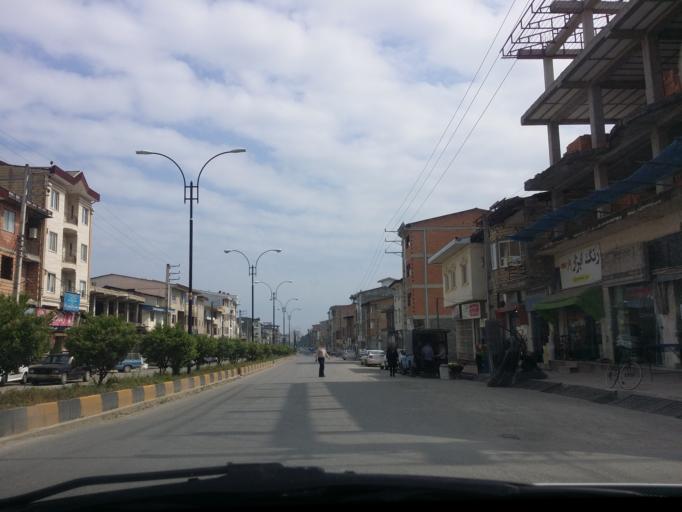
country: IR
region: Mazandaran
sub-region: Nowshahr
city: Nowshahr
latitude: 36.6317
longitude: 51.4862
